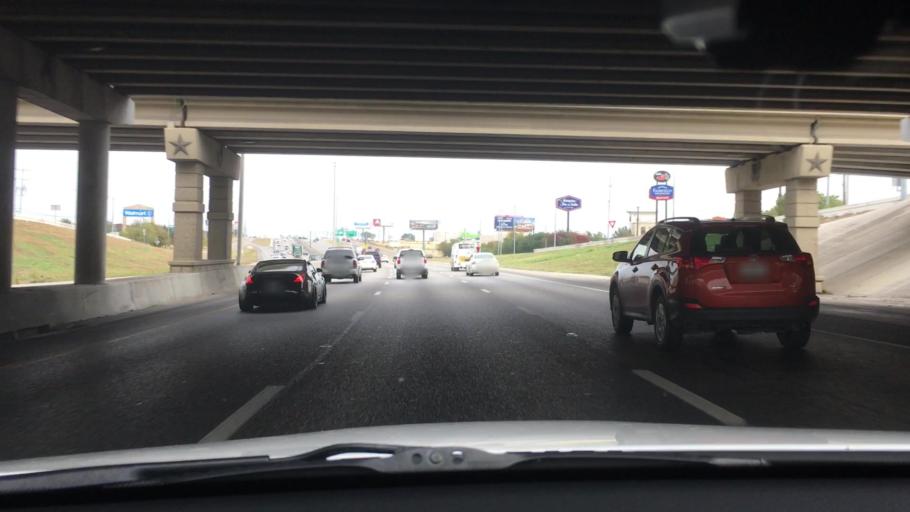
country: US
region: Texas
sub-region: Bexar County
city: Selma
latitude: 29.6004
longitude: -98.2769
